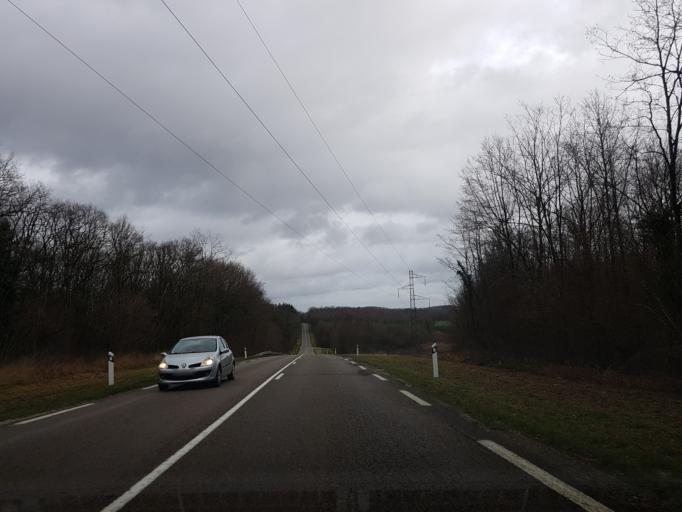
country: FR
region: Franche-Comte
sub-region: Departement de la Haute-Saone
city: Scey-sur-Saone-et-Saint-Albin
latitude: 47.6958
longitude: 5.9655
